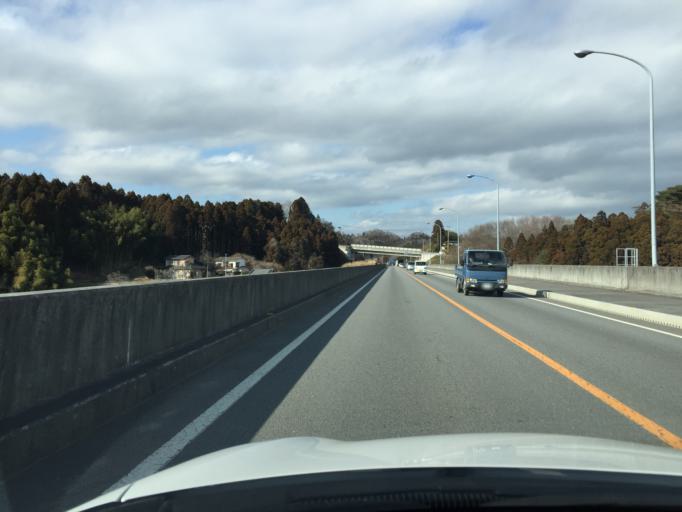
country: JP
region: Fukushima
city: Iwaki
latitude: 37.1430
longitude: 140.9903
